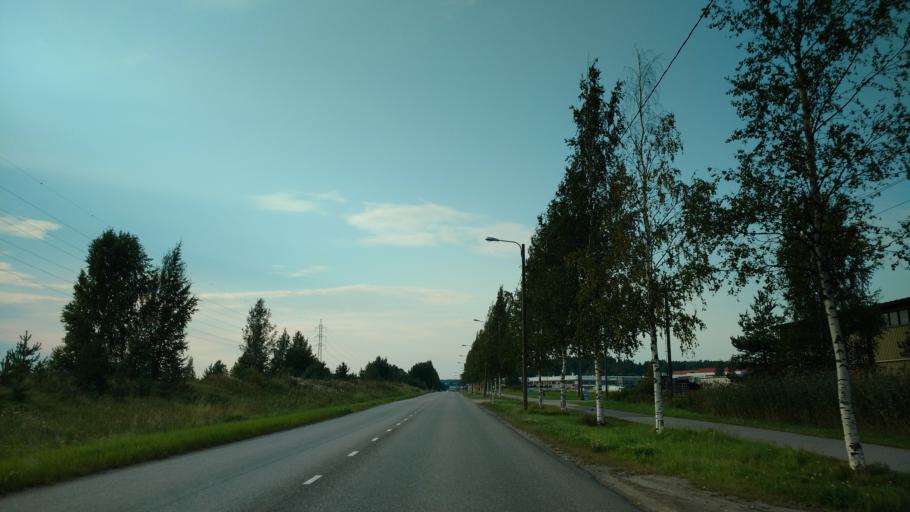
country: FI
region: Varsinais-Suomi
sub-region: Salo
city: Halikko
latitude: 60.3816
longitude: 23.1023
